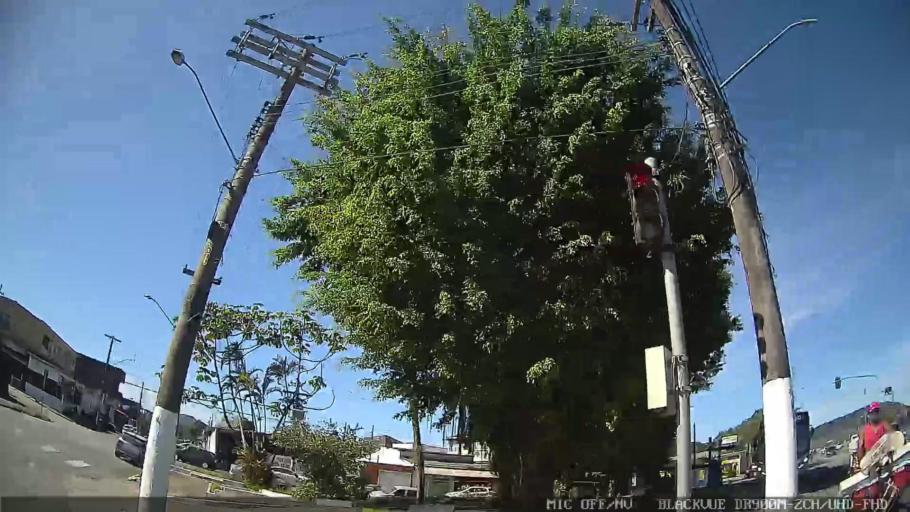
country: BR
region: Sao Paulo
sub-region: Guaruja
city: Guaruja
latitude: -23.9676
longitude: -46.2804
